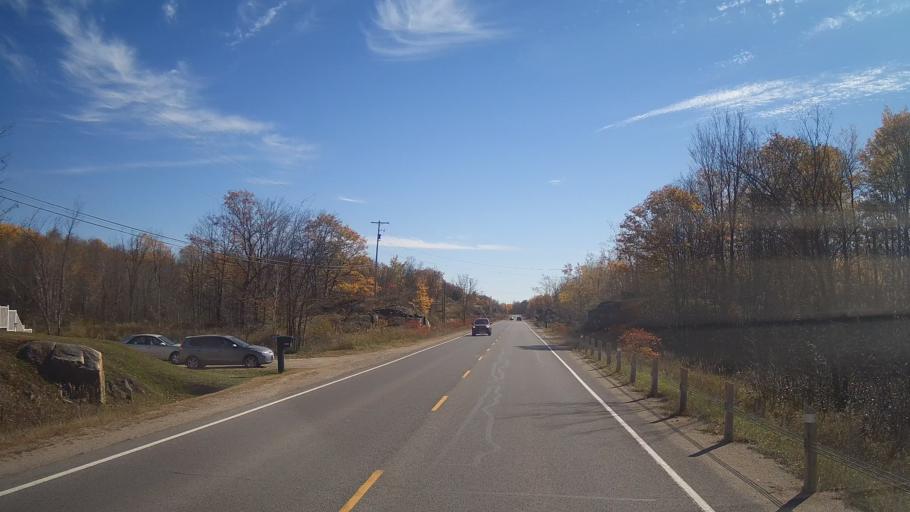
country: CA
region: Ontario
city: Perth
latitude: 44.7436
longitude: -76.6868
